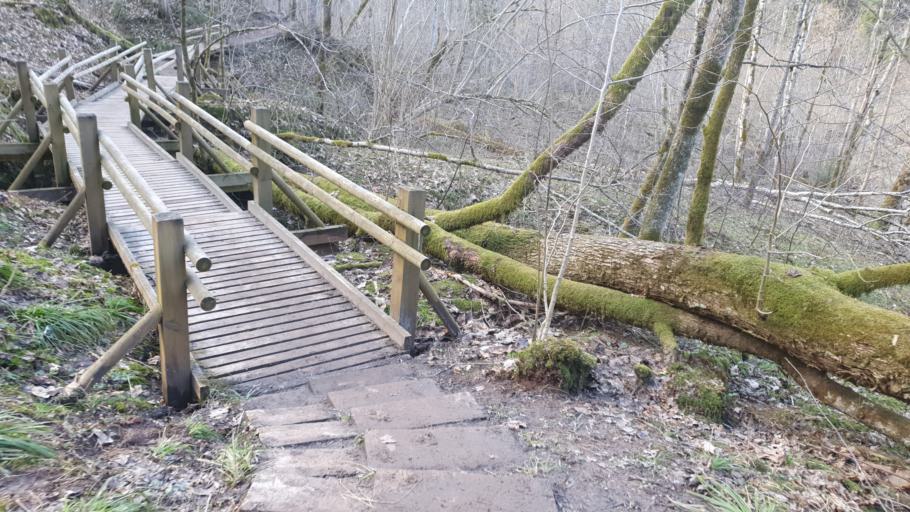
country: LV
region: Sigulda
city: Sigulda
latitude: 57.1724
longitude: 24.8727
